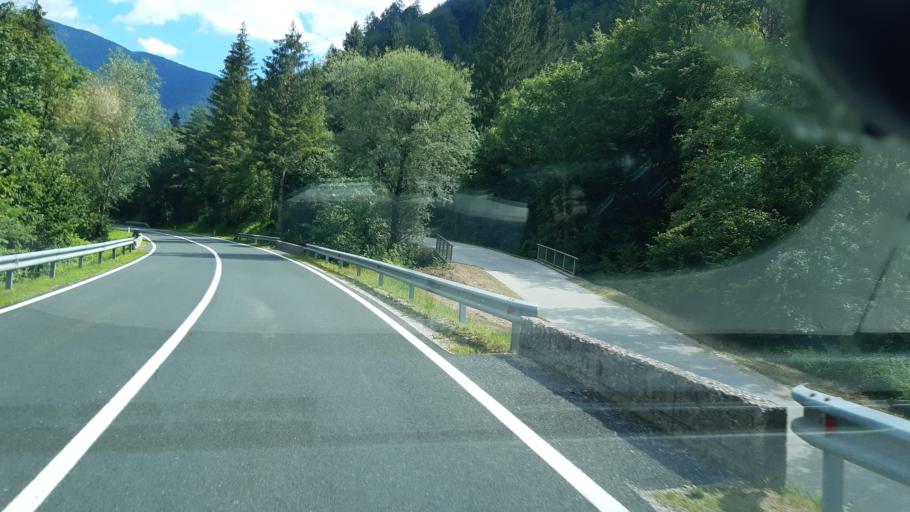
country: SI
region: Trzic
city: Trzic
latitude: 46.3865
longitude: 14.2911
